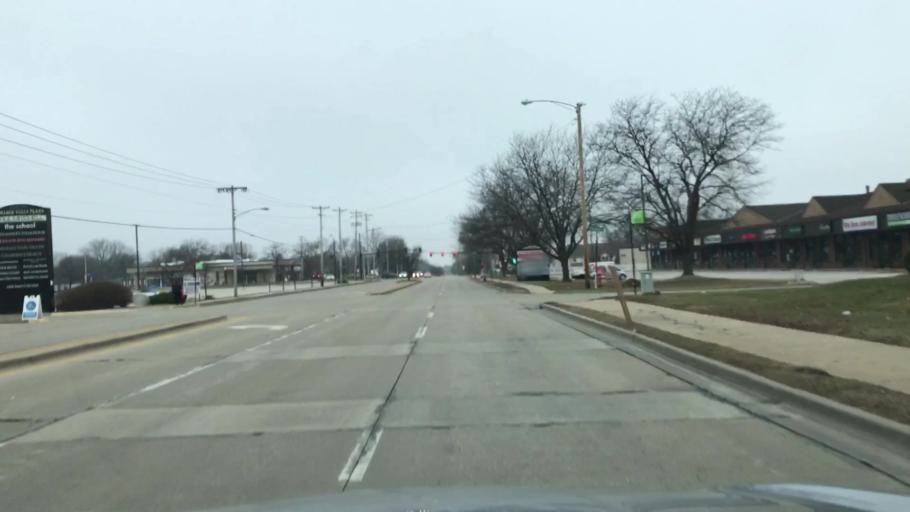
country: US
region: Illinois
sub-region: McLean County
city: Normal
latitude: 40.5104
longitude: -88.9580
